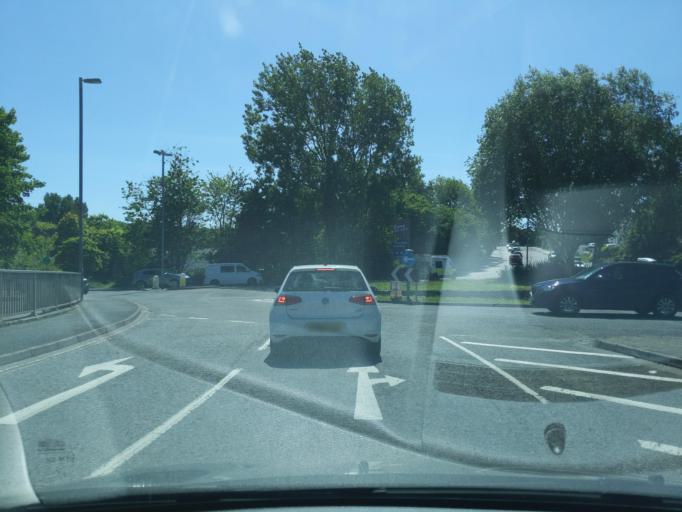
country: GB
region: England
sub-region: Cornwall
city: St Austell
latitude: 50.3352
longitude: -4.7760
